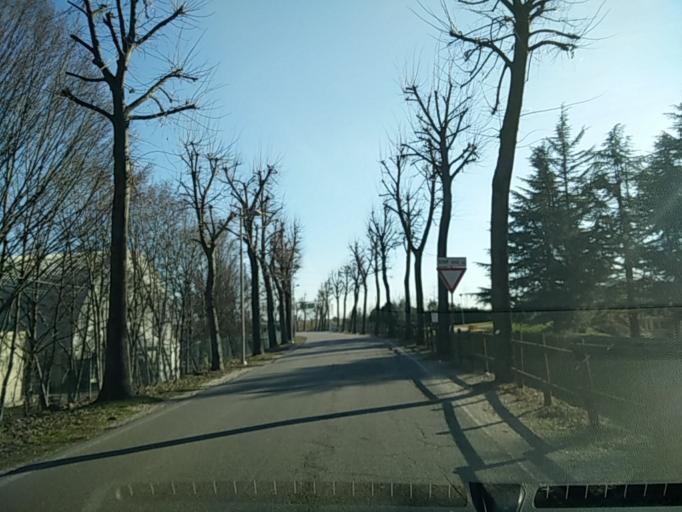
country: IT
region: Veneto
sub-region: Provincia di Treviso
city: San Vendemiano-Fossamerlo
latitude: 45.8887
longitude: 12.3387
